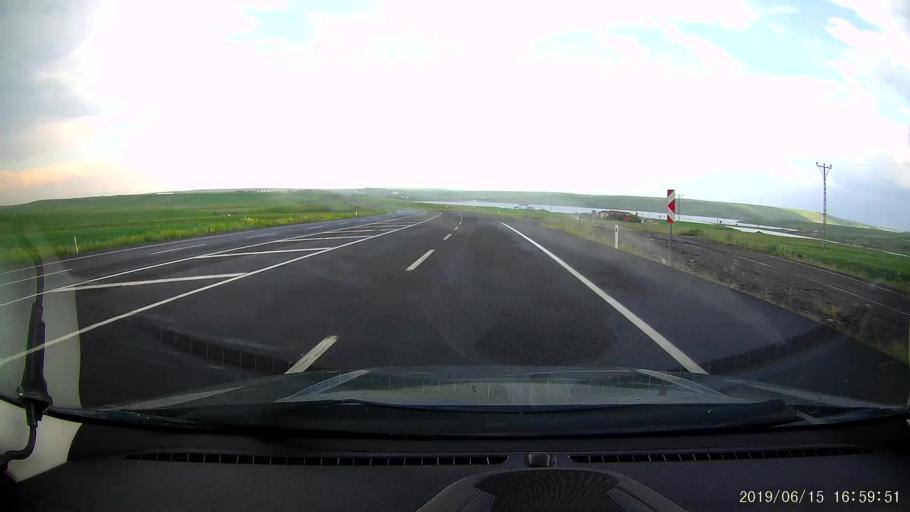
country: TR
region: Kars
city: Susuz
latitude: 40.7463
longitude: 43.1539
